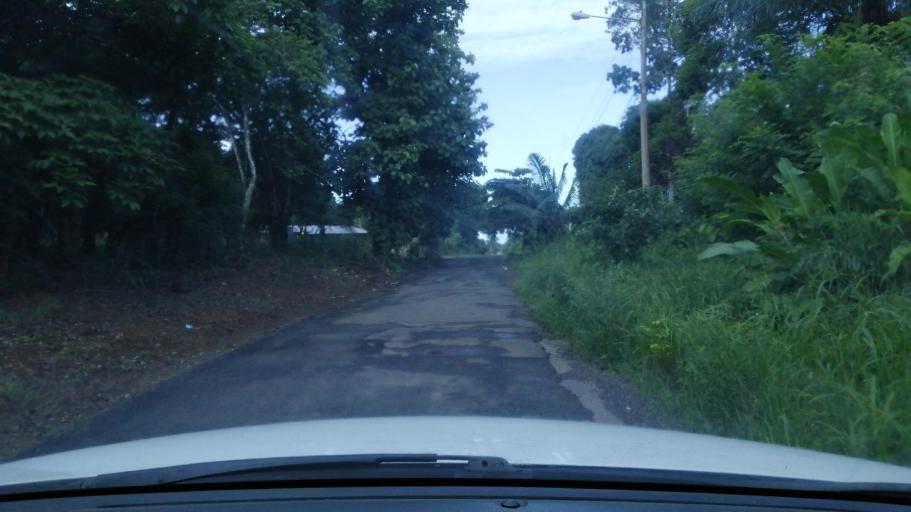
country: PA
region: Chiriqui
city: El Quiteno
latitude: 8.4707
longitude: -82.4119
